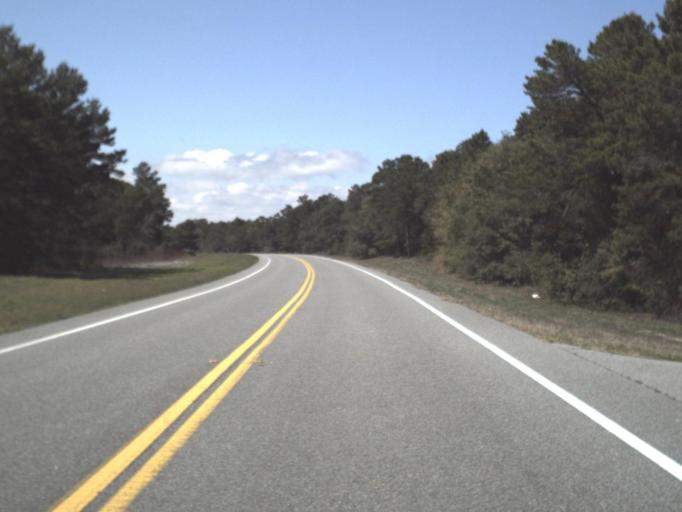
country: US
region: Florida
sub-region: Franklin County
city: Carrabelle
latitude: 29.9311
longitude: -84.4378
